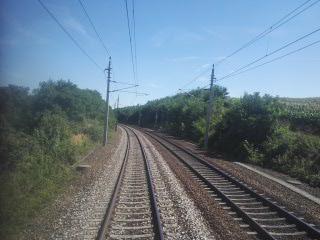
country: AT
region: Upper Austria
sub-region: Politischer Bezirk Grieskirchen
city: Bad Schallerbach
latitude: 48.2168
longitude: 13.9443
